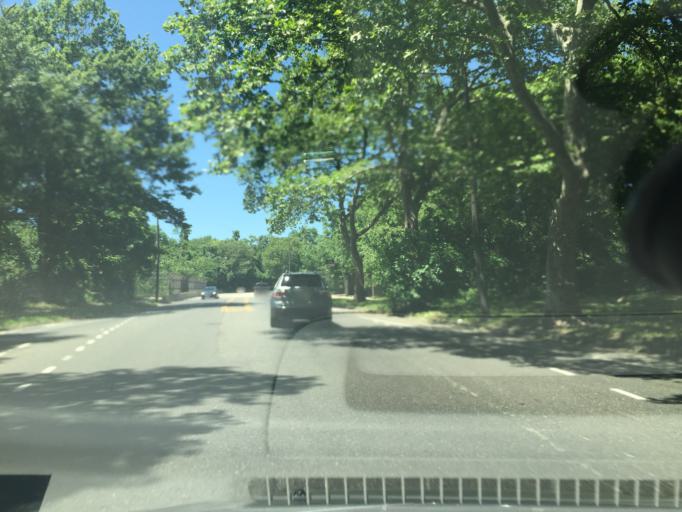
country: US
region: Pennsylvania
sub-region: Philadelphia County
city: Philadelphia
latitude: 39.9761
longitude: -75.1892
